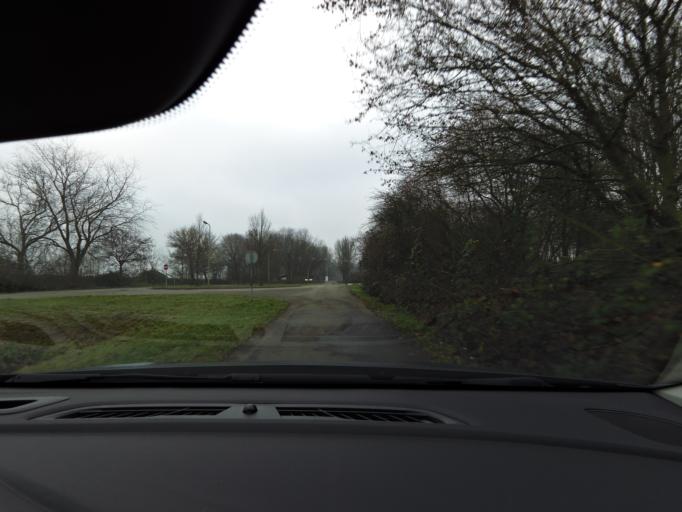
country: NL
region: South Holland
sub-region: Gemeente Maassluis
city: Maassluis
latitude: 51.8536
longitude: 4.2476
